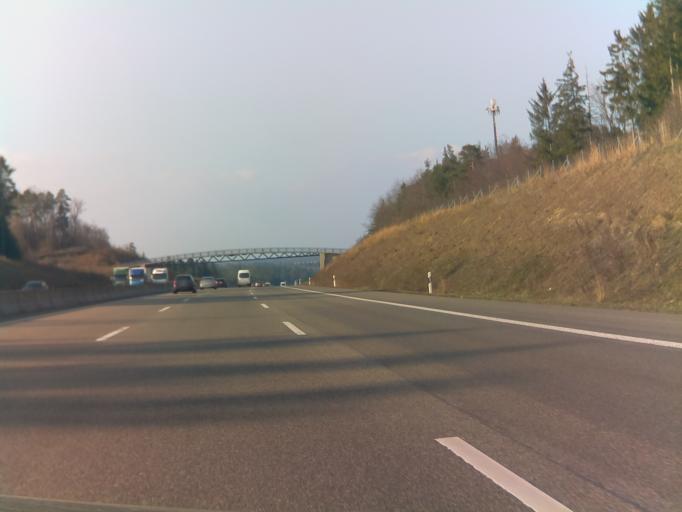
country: DE
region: Baden-Wuerttemberg
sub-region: Karlsruhe Region
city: Tiefenbronn
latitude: 48.8537
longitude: 8.7993
